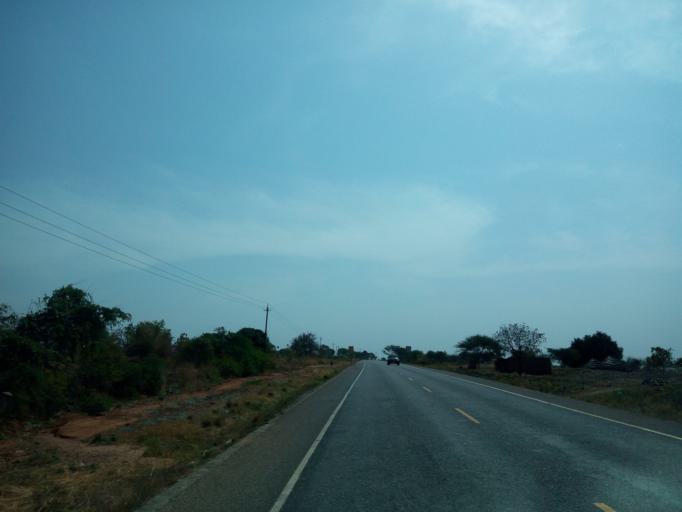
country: UG
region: Northern Region
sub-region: Nebbi District
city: Nebbi
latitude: 2.4648
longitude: 31.3500
